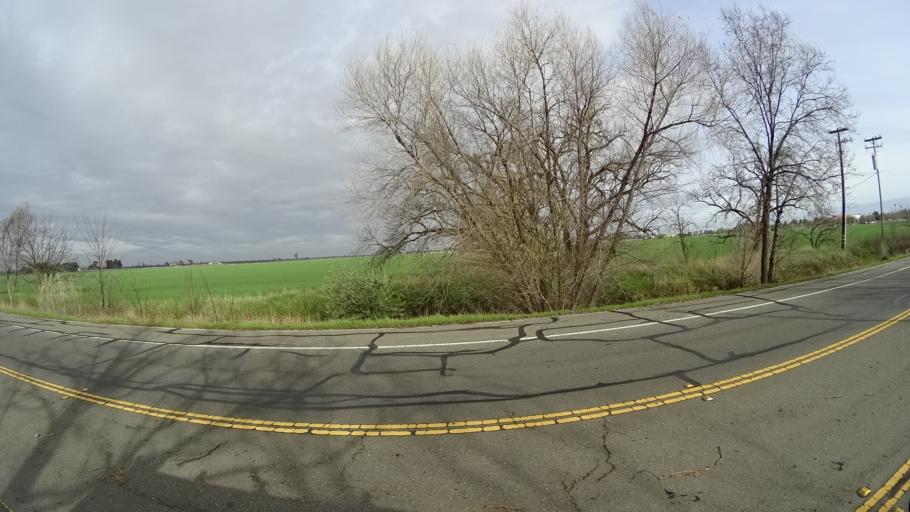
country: US
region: California
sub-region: Yolo County
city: Davis
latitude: 38.5609
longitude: -121.7772
